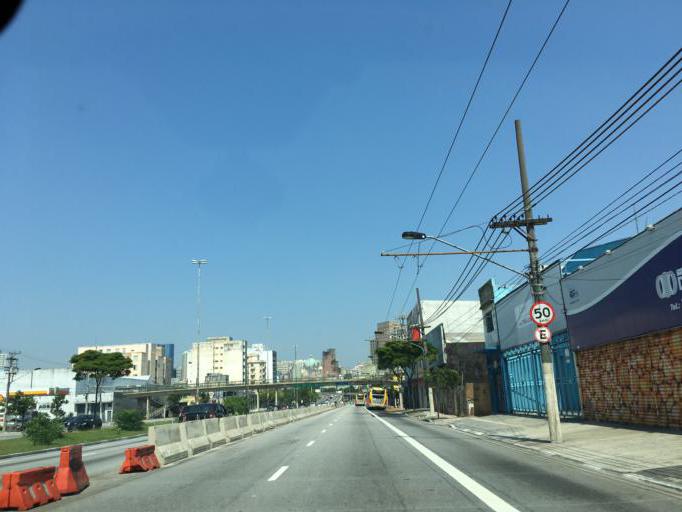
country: BR
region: Sao Paulo
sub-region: Sao Paulo
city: Sao Paulo
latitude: -23.5521
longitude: -46.6205
